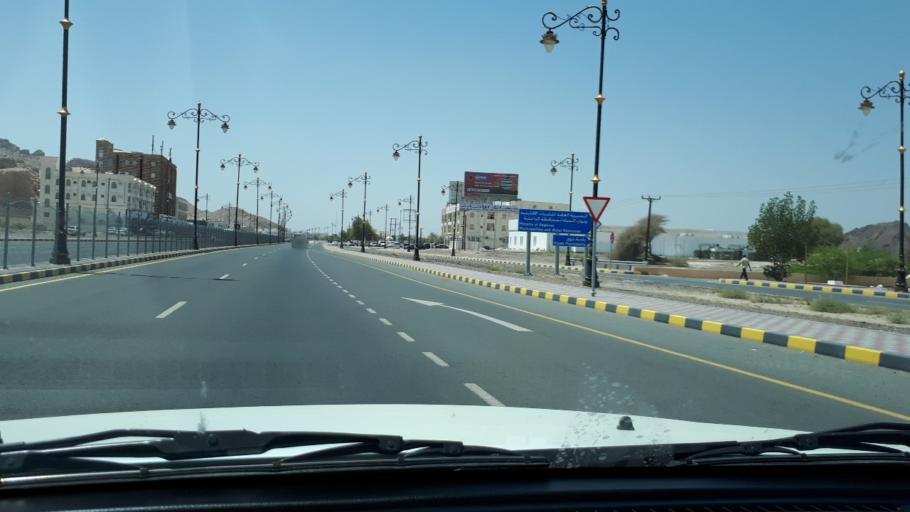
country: OM
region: Muhafazat ad Dakhiliyah
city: Nizwa
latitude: 22.9016
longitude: 57.5326
